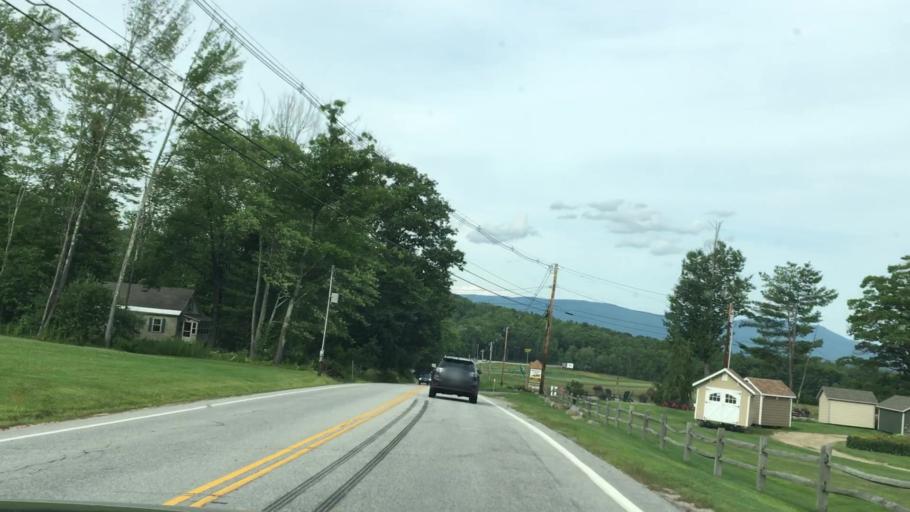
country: US
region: New Hampshire
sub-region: Belknap County
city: Meredith
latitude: 43.6781
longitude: -71.4737
